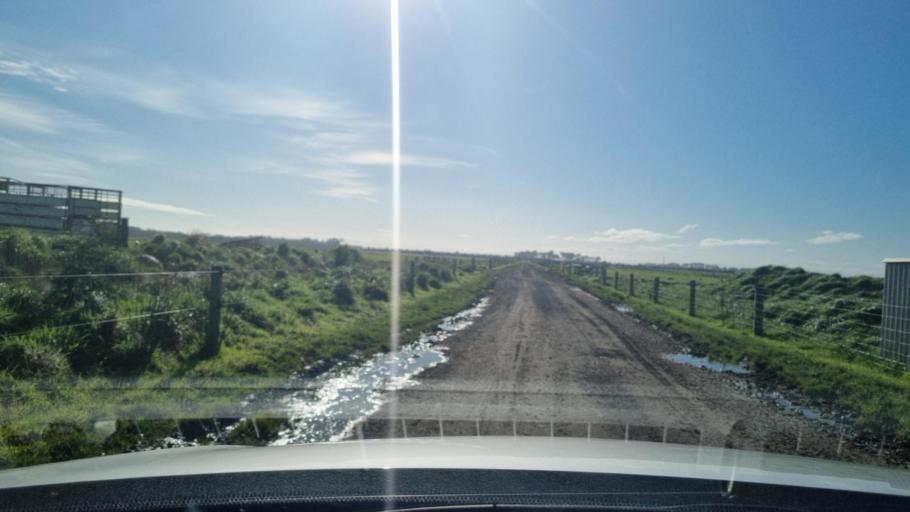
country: NZ
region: Southland
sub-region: Invercargill City
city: Invercargill
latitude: -46.4209
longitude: 168.3105
